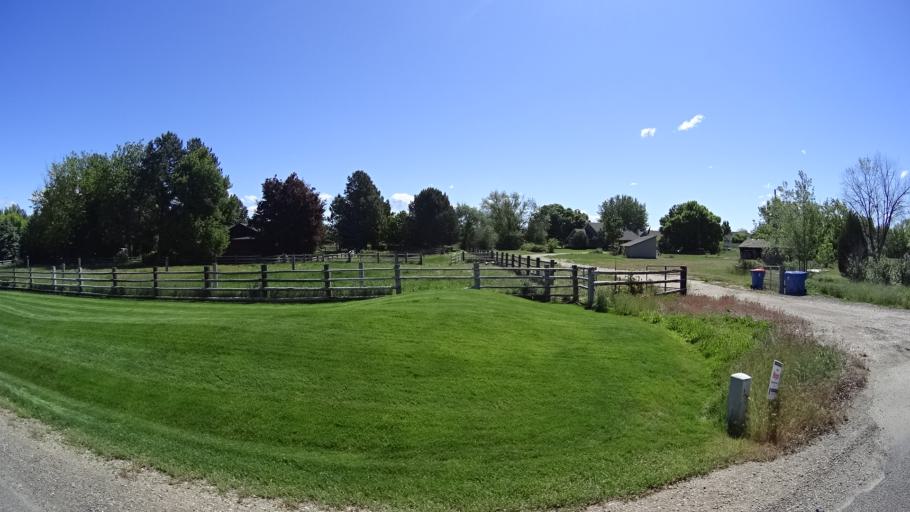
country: US
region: Idaho
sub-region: Ada County
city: Eagle
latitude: 43.6567
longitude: -116.3745
